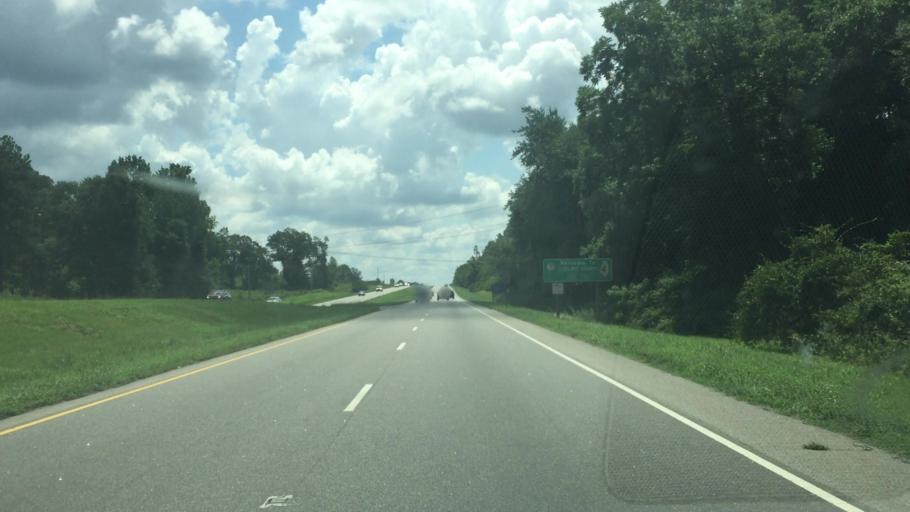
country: US
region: North Carolina
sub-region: Richmond County
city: Hamlet
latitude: 34.8543
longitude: -79.6231
